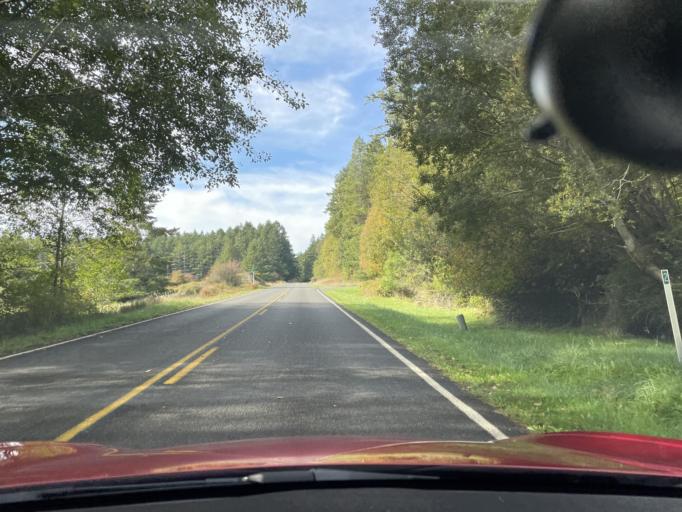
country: US
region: Washington
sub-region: San Juan County
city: Friday Harbor
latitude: 48.5290
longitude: -122.9838
